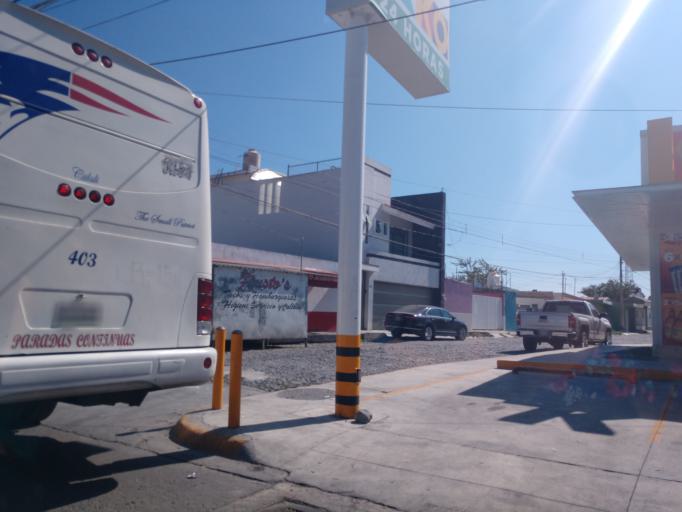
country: MX
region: Nayarit
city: Xalisco
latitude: 21.4688
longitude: -104.8748
